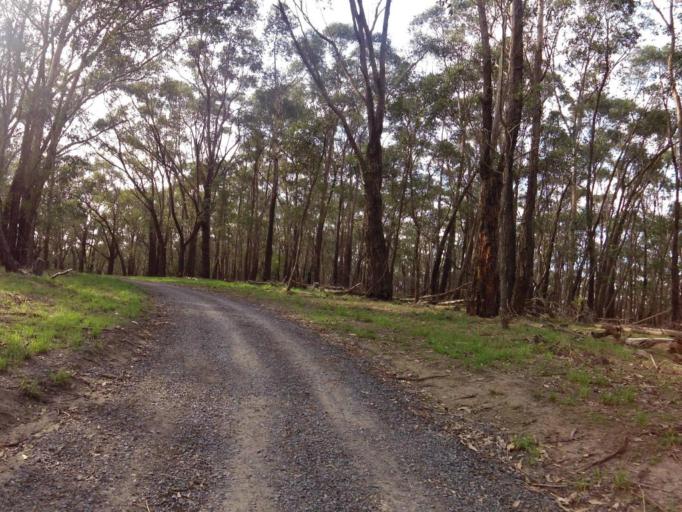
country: AU
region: Victoria
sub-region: Yarra Ranges
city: Lysterfield
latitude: -37.9453
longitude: 145.3043
